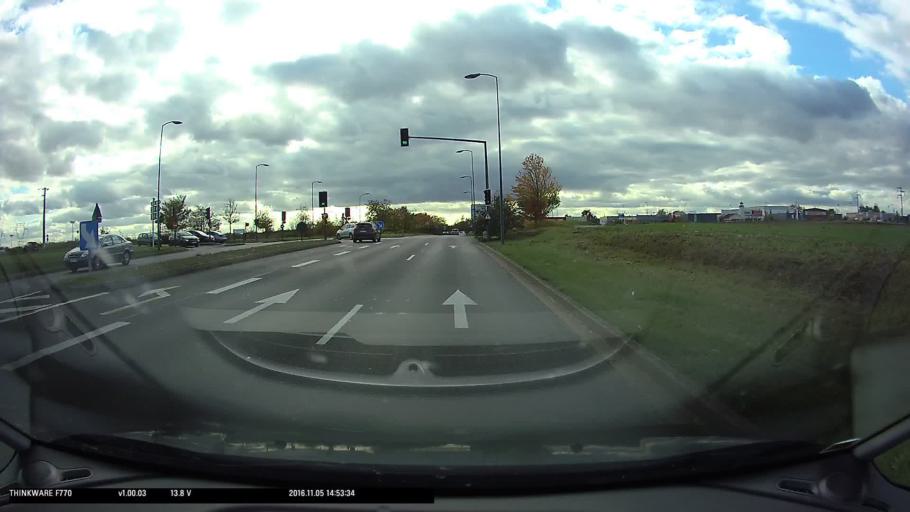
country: FR
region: Ile-de-France
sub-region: Departement du Val-d'Oise
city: Ennery
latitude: 49.0721
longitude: 2.0843
